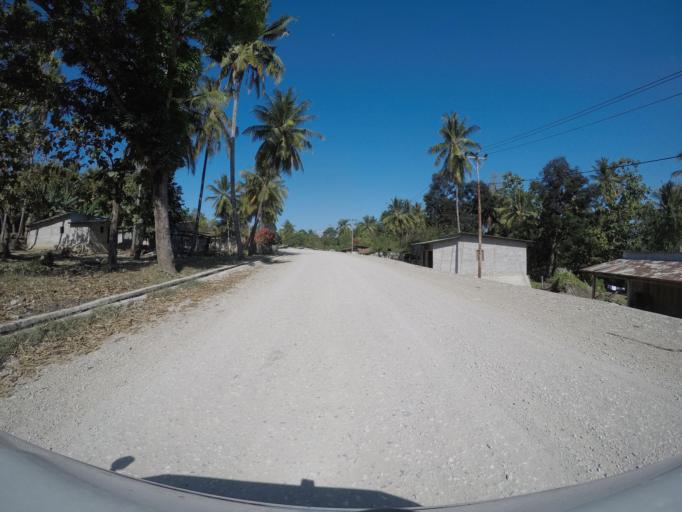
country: TL
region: Viqueque
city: Viqueque
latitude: -8.8423
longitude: 126.5144
